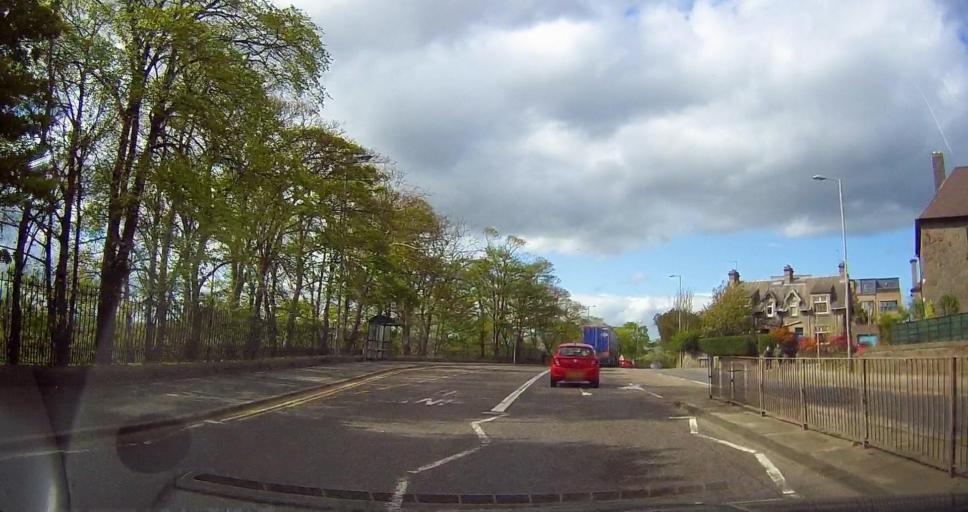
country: GB
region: Scotland
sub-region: Aberdeen City
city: Aberdeen
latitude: 57.1311
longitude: -2.0942
